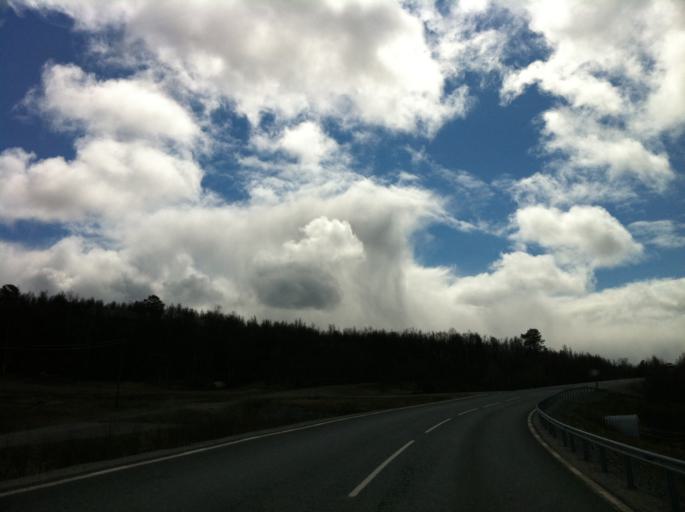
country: NO
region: Sor-Trondelag
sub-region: Tydal
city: Aas
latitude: 62.6464
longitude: 12.4276
